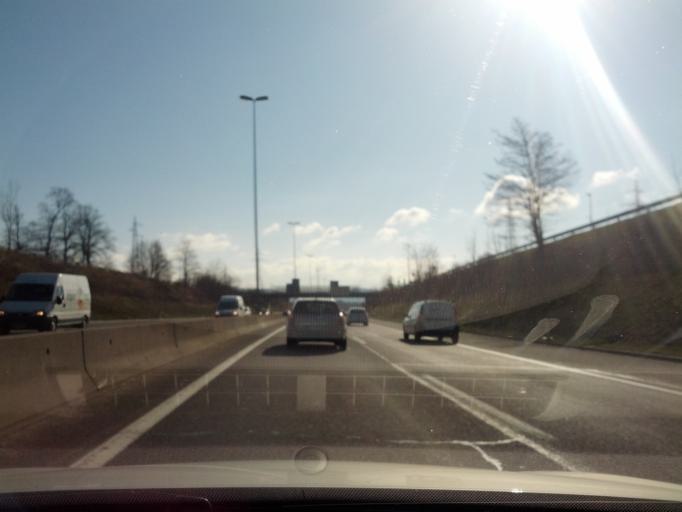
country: SI
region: Ljubljana
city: Ljubljana
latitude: 46.0772
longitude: 14.5384
